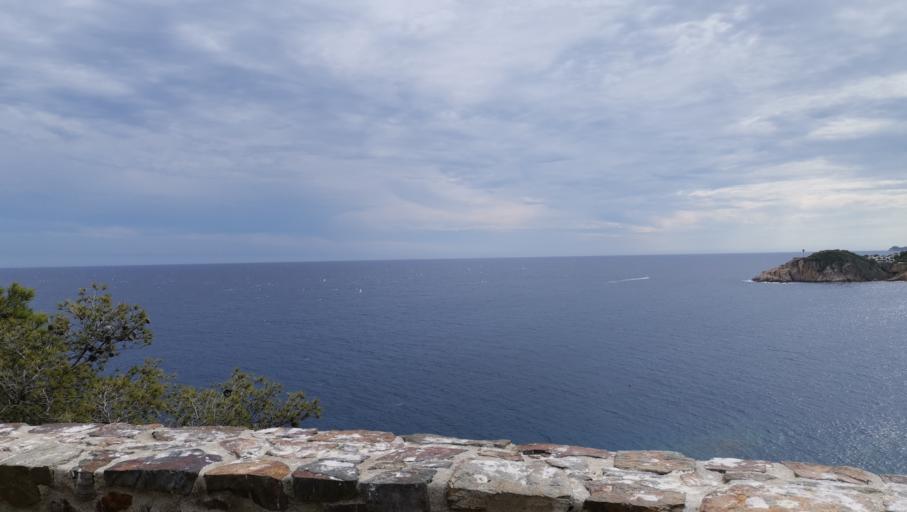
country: ES
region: Catalonia
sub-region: Provincia de Girona
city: Sant Feliu de Guixols
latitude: 41.7786
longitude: 3.0406
